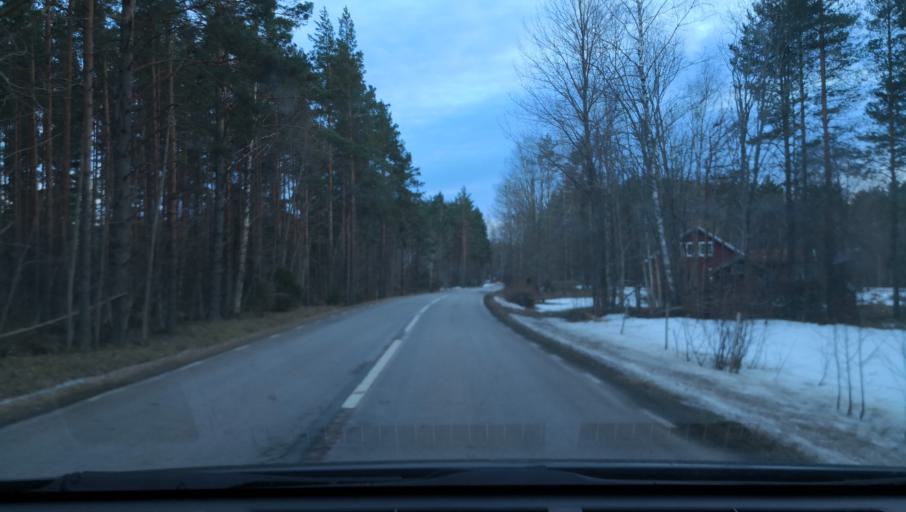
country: SE
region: Uppsala
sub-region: Osthammars Kommun
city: Osterbybruk
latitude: 60.2723
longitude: 17.9578
